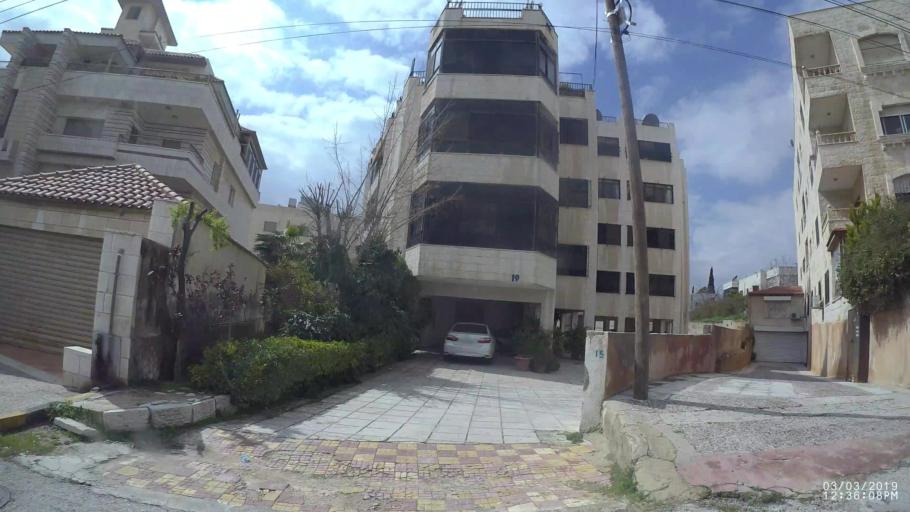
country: JO
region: Amman
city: Amman
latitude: 31.9742
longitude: 35.9025
